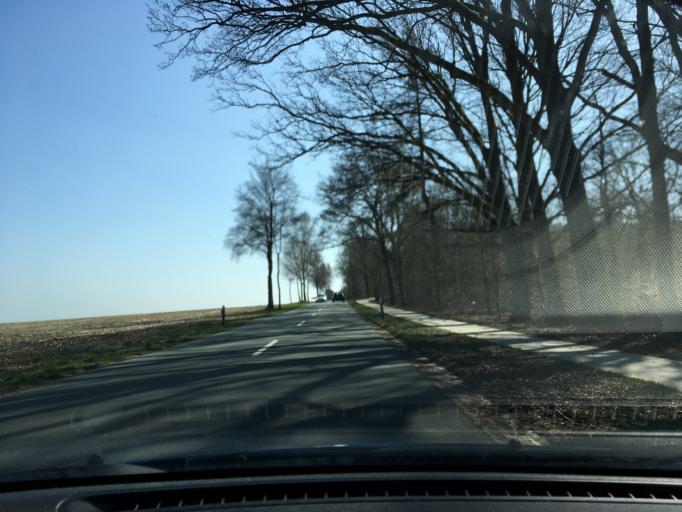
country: DE
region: Lower Saxony
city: Eimke
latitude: 52.9866
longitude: 10.3073
